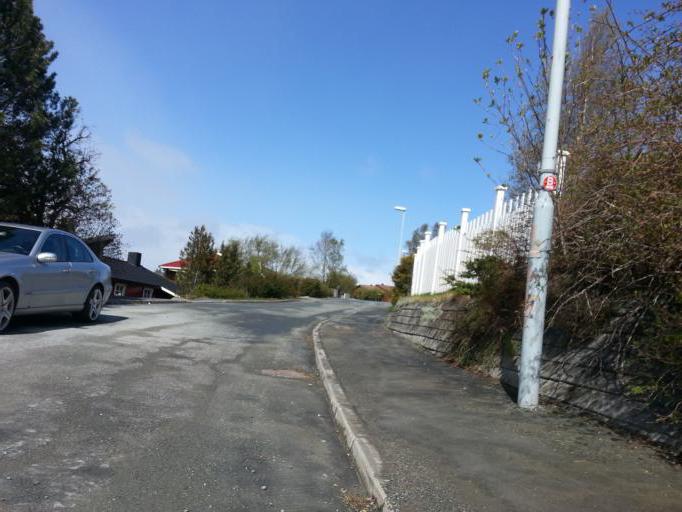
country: NO
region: Sor-Trondelag
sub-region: Trondheim
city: Trondheim
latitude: 63.3890
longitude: 10.3623
